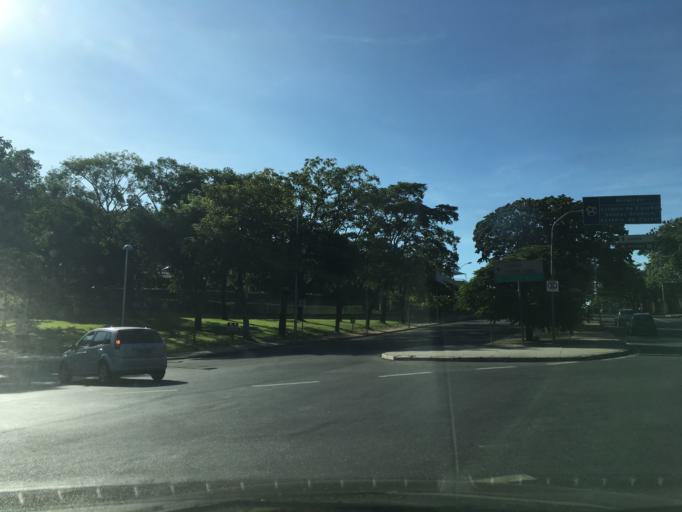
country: BR
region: Minas Gerais
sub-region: Belo Horizonte
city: Belo Horizonte
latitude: -19.8641
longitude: -43.9739
